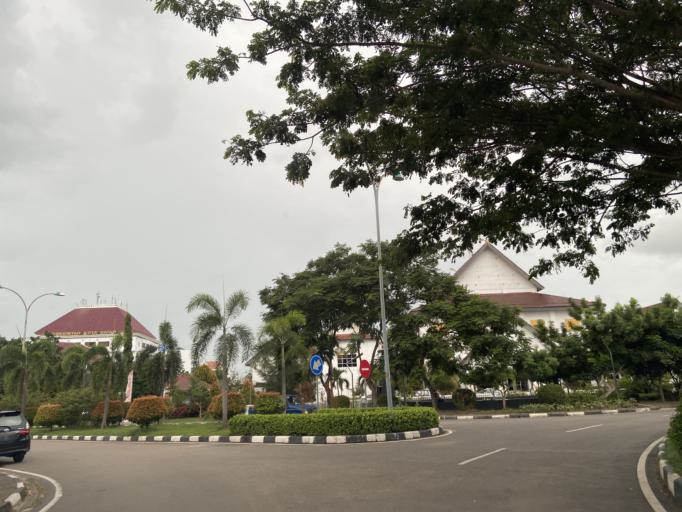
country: SG
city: Singapore
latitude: 1.1261
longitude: 104.0544
